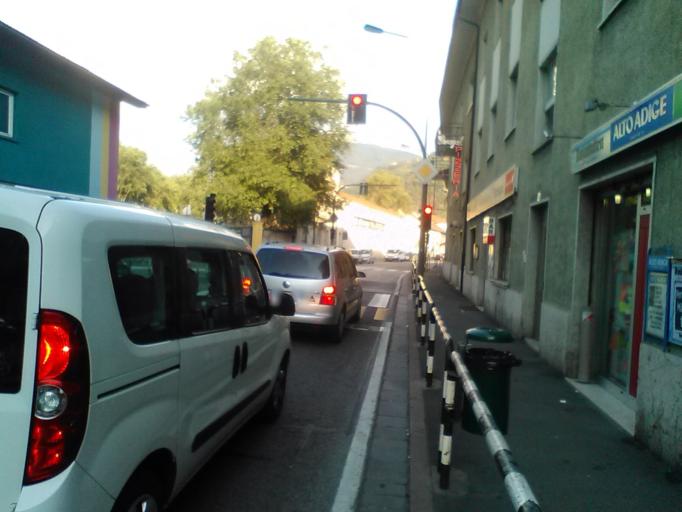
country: IT
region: Trentino-Alto Adige
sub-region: Bolzano
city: Bolzano
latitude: 46.4979
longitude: 11.3659
